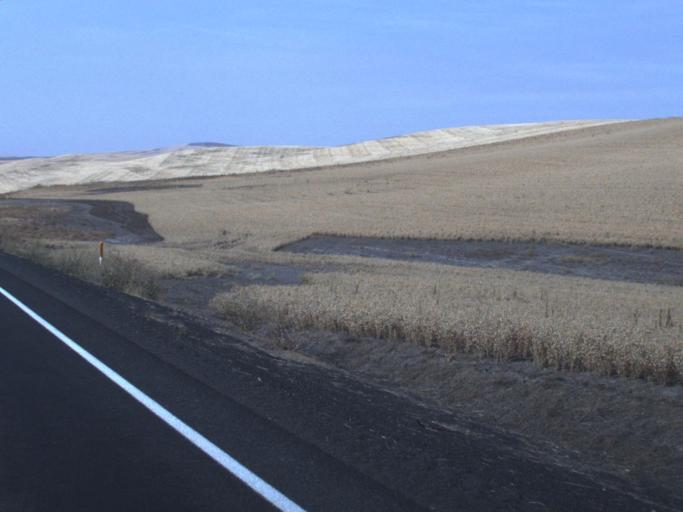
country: US
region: Washington
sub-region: Whitman County
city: Pullman
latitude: 46.8958
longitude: -117.1030
